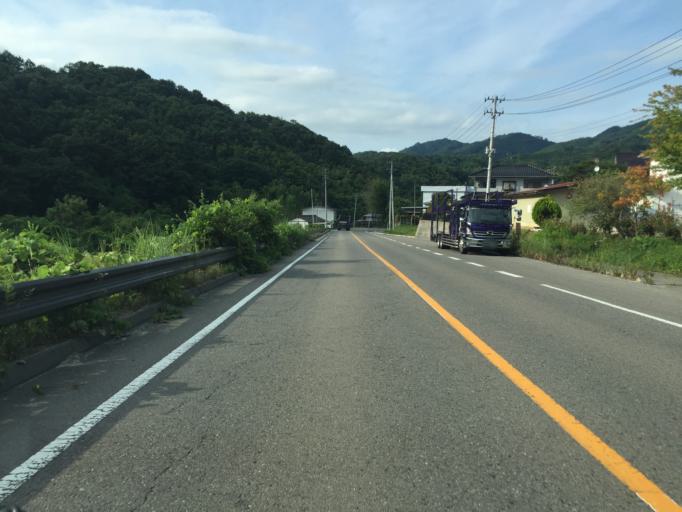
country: JP
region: Fukushima
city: Hobaramachi
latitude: 37.6803
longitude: 140.6159
